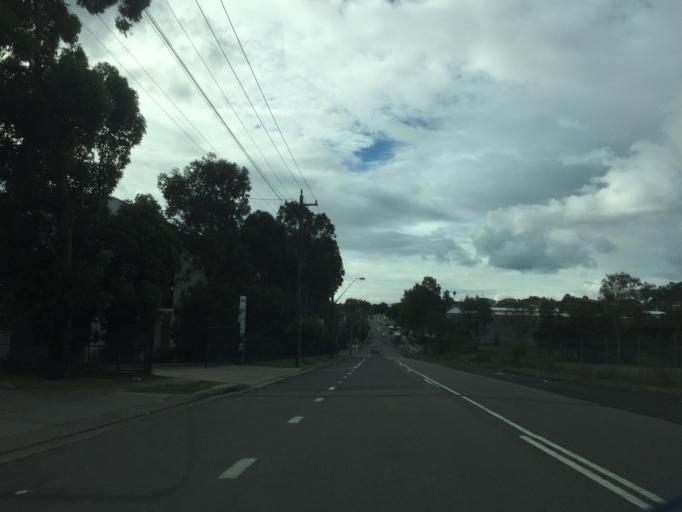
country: AU
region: New South Wales
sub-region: Blacktown
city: Doonside
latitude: -33.7937
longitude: 150.8897
